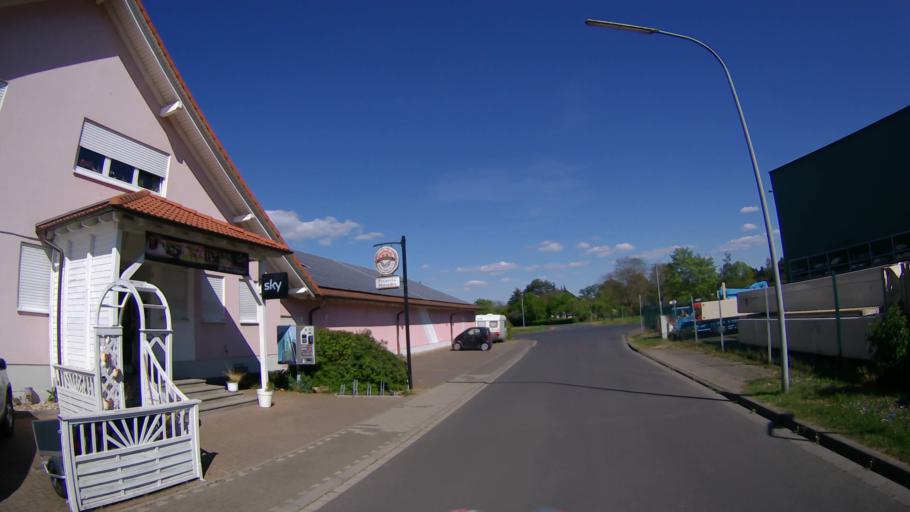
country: DE
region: Hesse
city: Hain-Grundau
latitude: 50.1999
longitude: 9.1200
